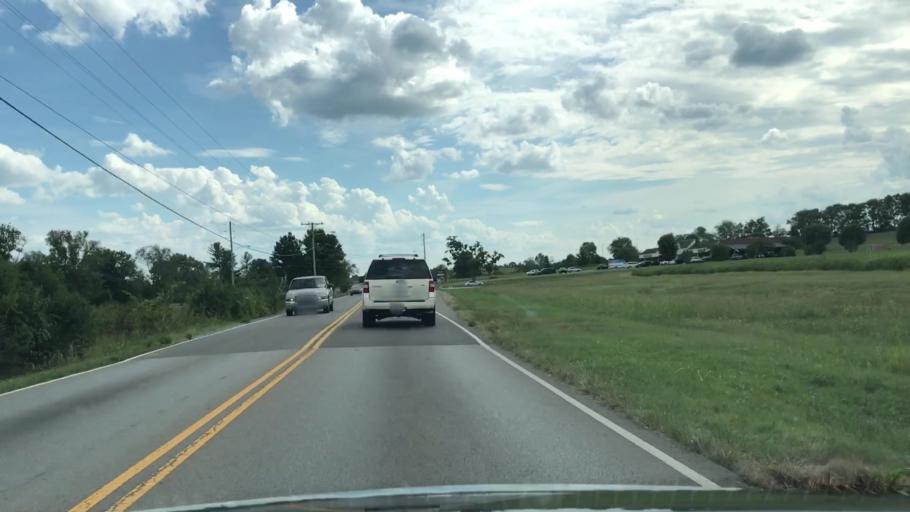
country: US
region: Tennessee
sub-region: Maury County
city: Spring Hill
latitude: 35.7390
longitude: -86.9247
